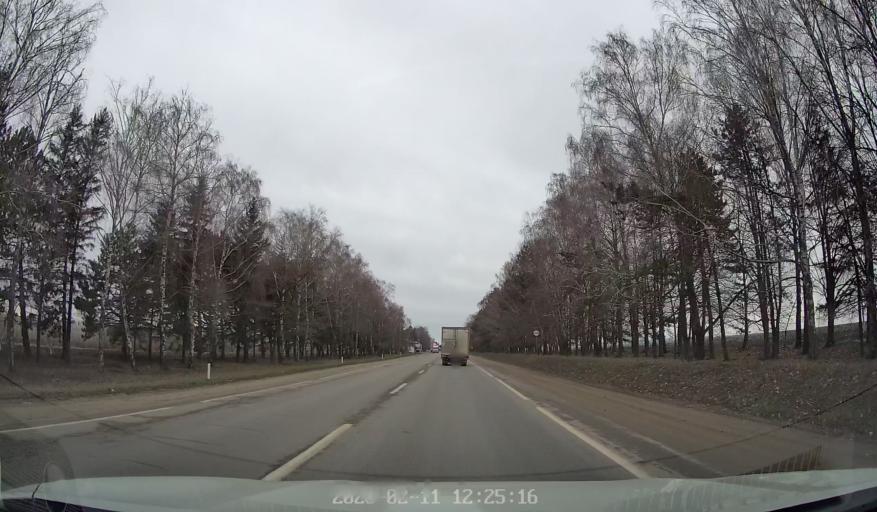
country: MD
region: Raionul Edinet
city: Edinet
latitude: 48.1537
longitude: 27.3373
